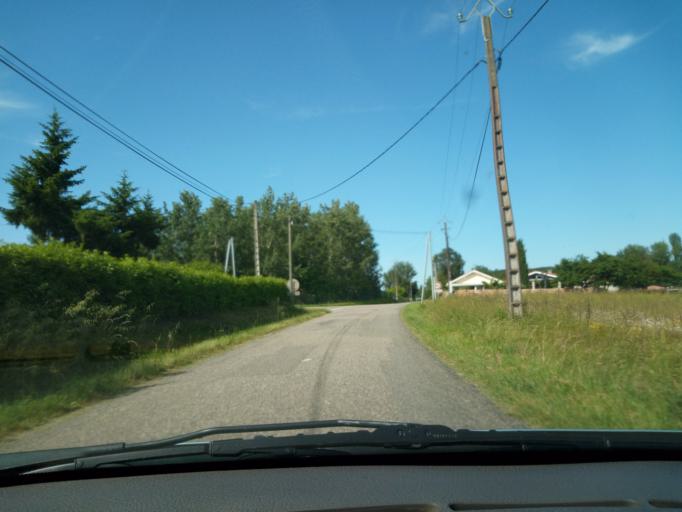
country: FR
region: Midi-Pyrenees
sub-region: Departement du Tarn-et-Garonne
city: Molieres
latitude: 44.2177
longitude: 1.3240
